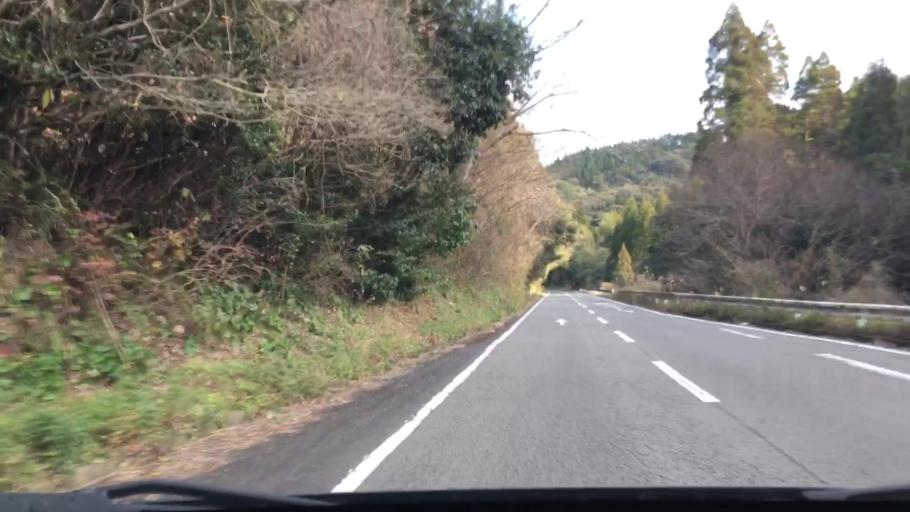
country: JP
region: Miyazaki
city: Nichinan
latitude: 31.5911
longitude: 131.3029
